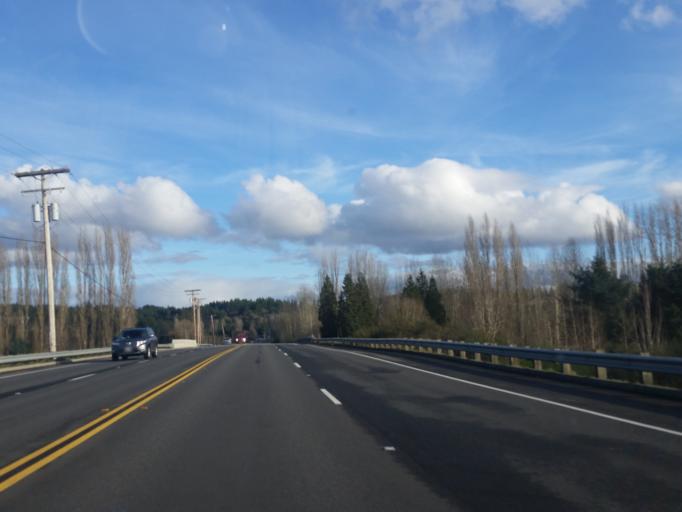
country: US
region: Washington
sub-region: King County
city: Kingsgate
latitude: 47.7112
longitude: -122.1445
